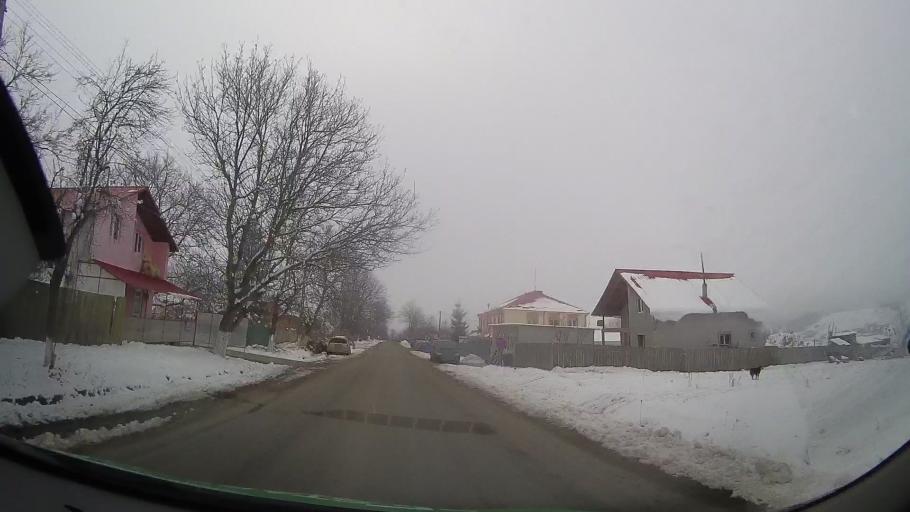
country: RO
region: Bacau
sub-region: Comuna Stanisesti
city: Stanisesti
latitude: 46.4058
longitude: 27.2725
